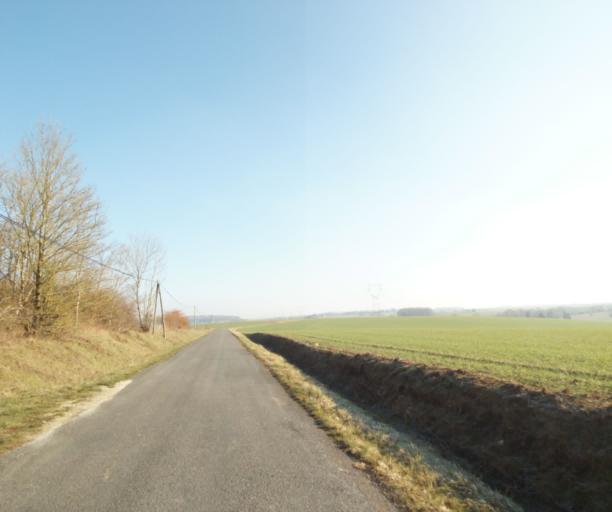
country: FR
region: Champagne-Ardenne
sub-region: Departement de la Haute-Marne
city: Wassy
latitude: 48.5190
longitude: 4.9784
